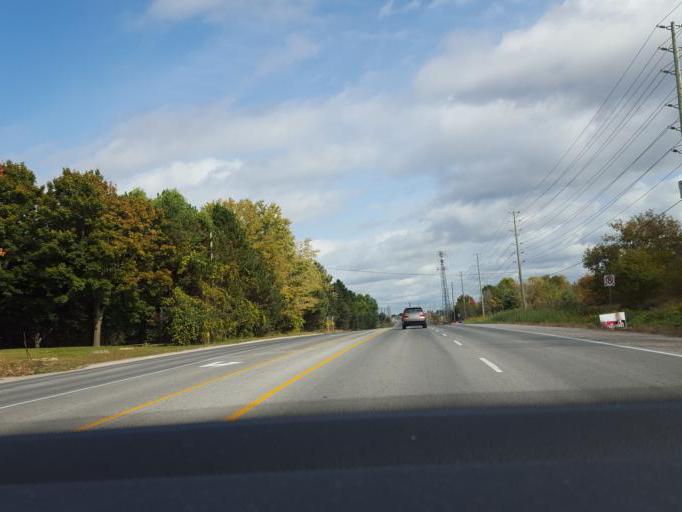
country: CA
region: Ontario
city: Ajax
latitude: 43.9029
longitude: -79.0102
